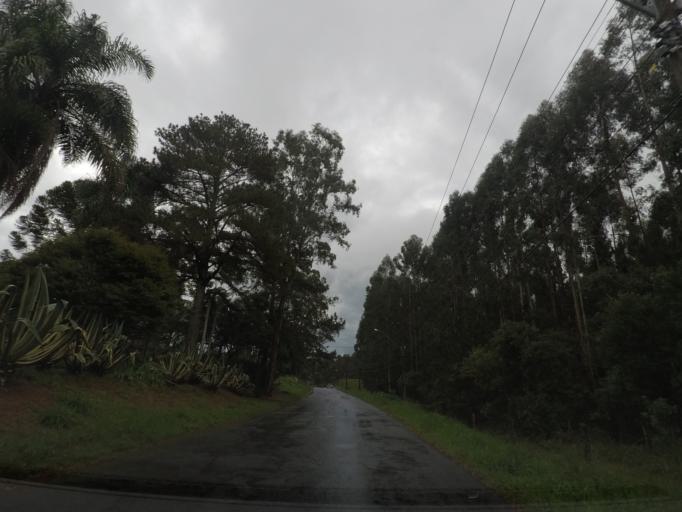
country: BR
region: Parana
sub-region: Campo Largo
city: Campo Largo
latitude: -25.4559
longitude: -49.4361
